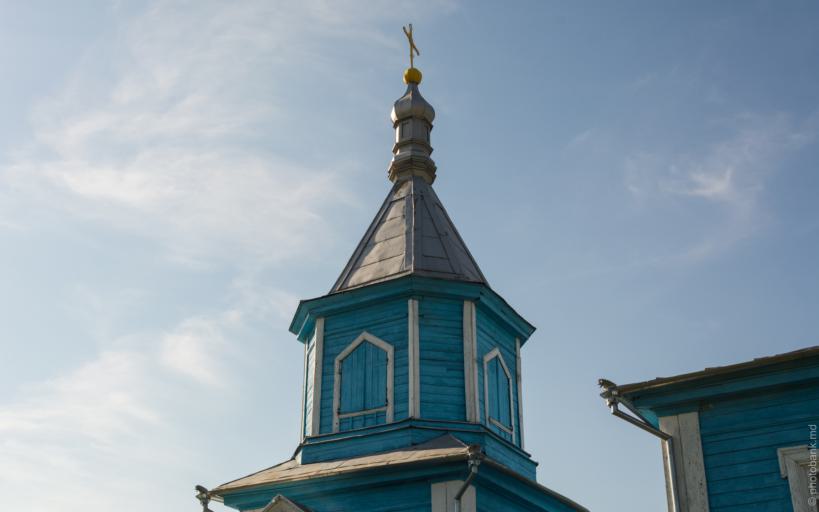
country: MD
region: Balti
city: Balti
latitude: 47.7072
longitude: 27.8695
